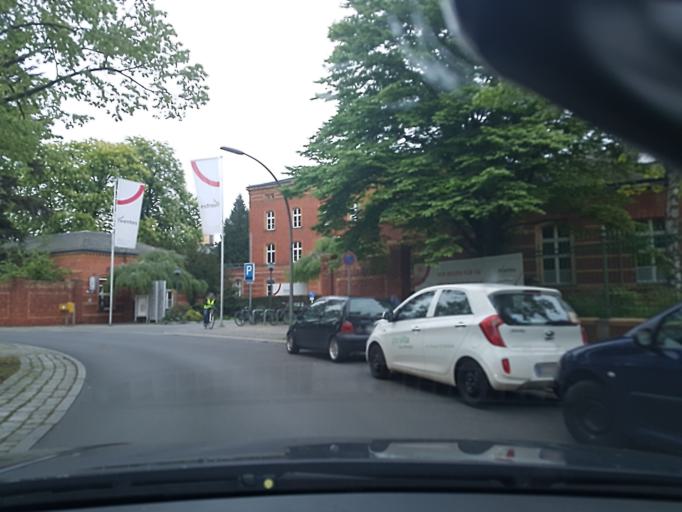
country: DE
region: Berlin
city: Tempelhof Bezirk
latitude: 52.4588
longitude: 13.3876
